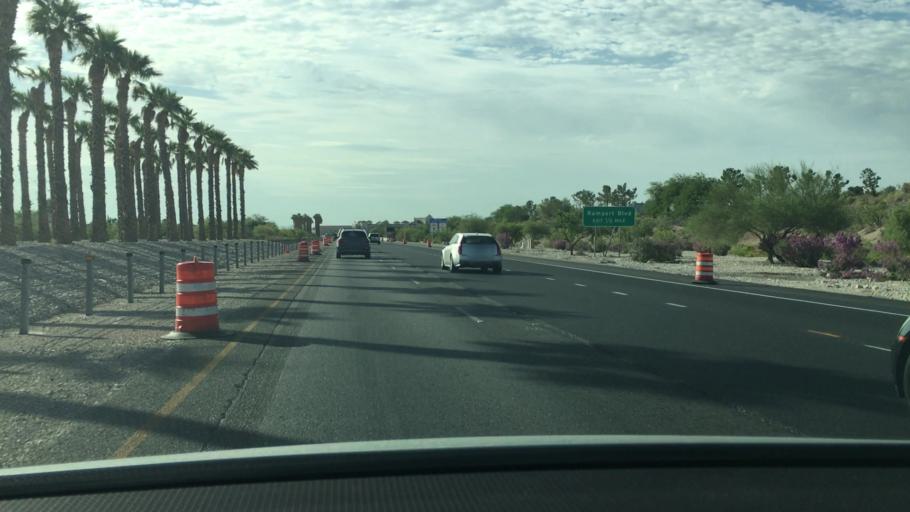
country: US
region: Nevada
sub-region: Clark County
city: Summerlin South
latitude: 36.1835
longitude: -115.3022
